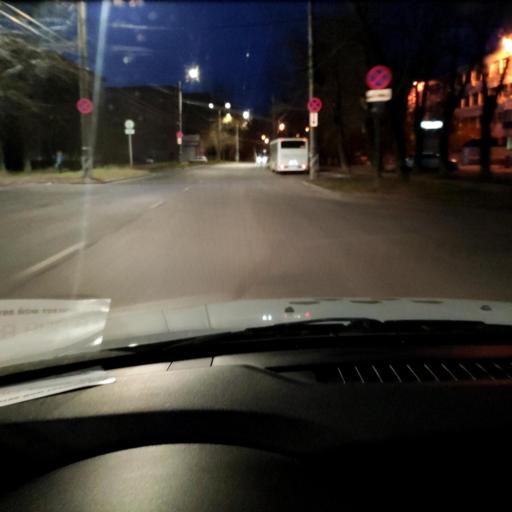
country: RU
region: Samara
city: Tol'yatti
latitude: 53.5151
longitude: 49.4556
